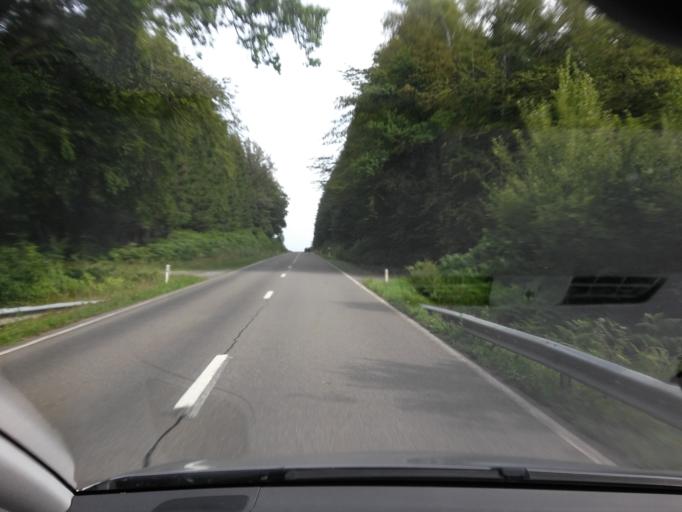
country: BE
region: Wallonia
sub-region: Province du Luxembourg
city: Chiny
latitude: 49.7541
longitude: 5.3148
